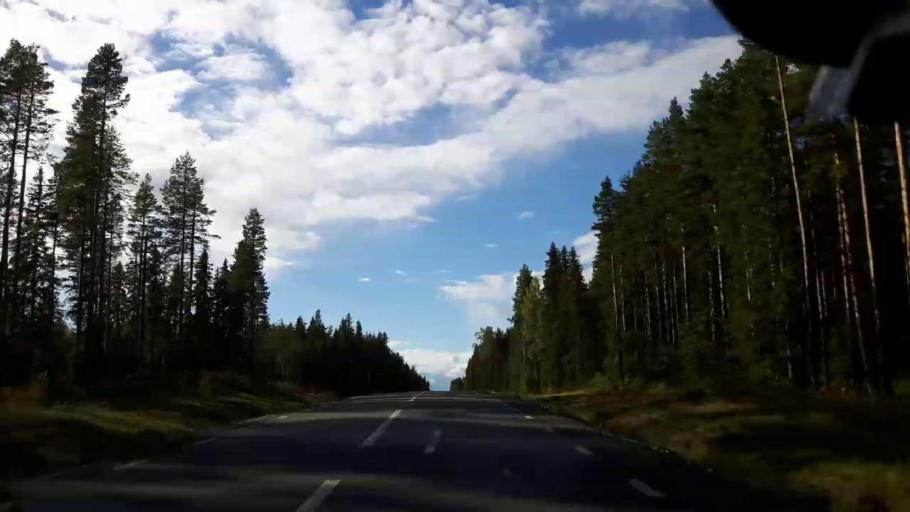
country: SE
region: Jaemtland
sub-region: Stroemsunds Kommun
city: Stroemsund
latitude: 63.5634
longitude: 15.7967
